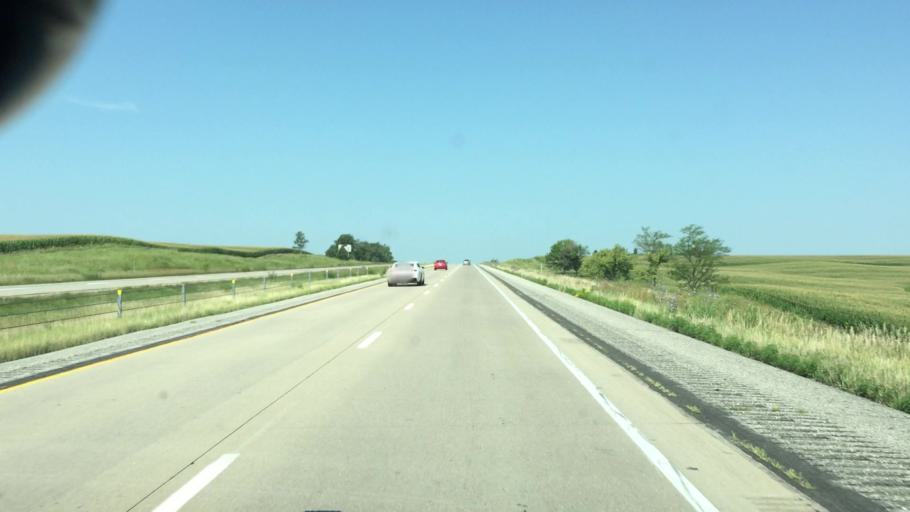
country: US
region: Iowa
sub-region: Iowa County
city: Williamsburg
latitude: 41.6916
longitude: -92.0960
